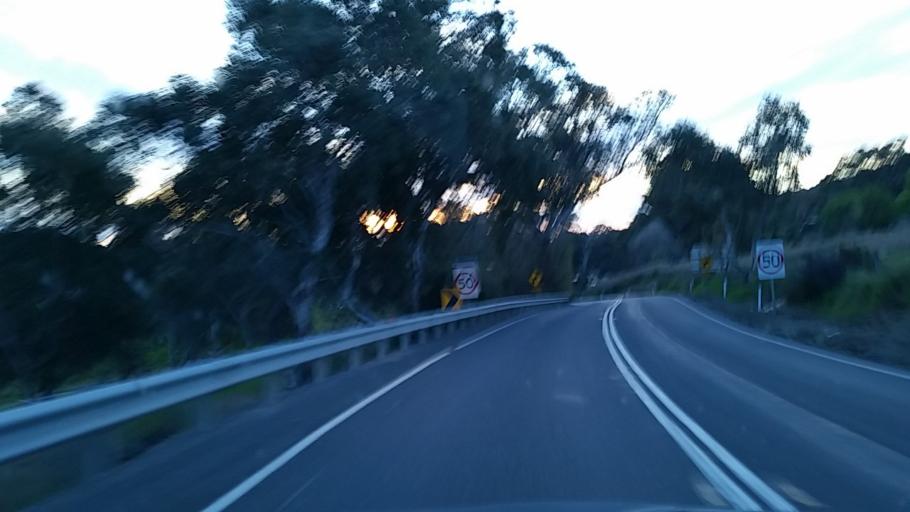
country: AU
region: South Australia
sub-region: Yankalilla
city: Normanville
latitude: -35.4573
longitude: 138.3531
